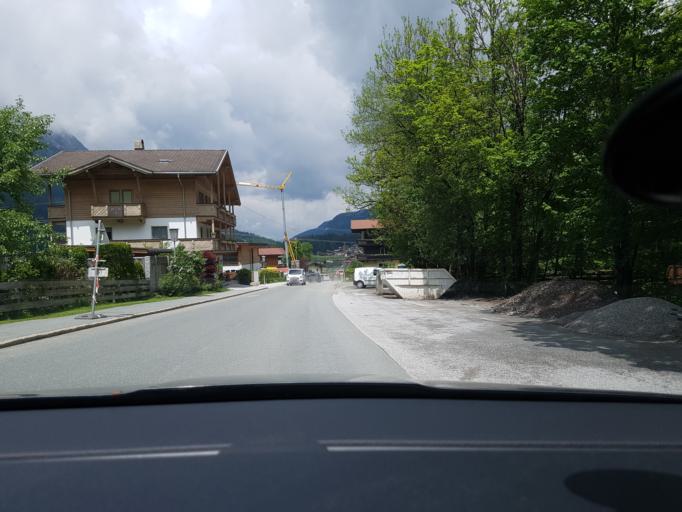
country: AT
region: Tyrol
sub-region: Politischer Bezirk Kufstein
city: Soll
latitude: 47.4983
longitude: 12.1981
